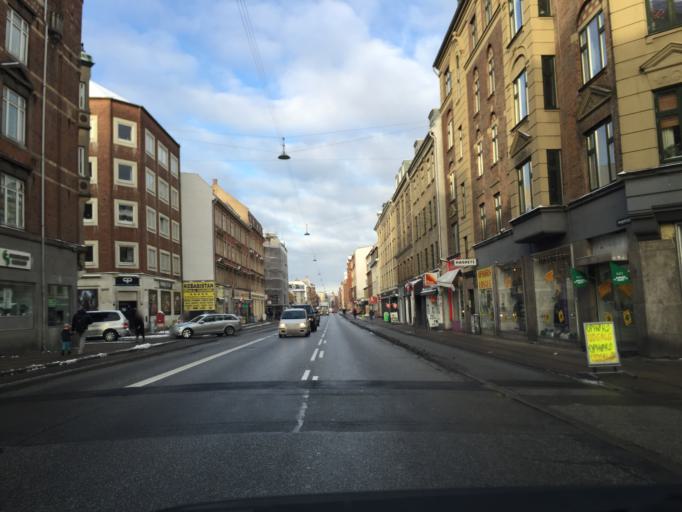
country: DK
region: Capital Region
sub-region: Kobenhavn
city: Christianshavn
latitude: 55.6587
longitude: 12.6072
